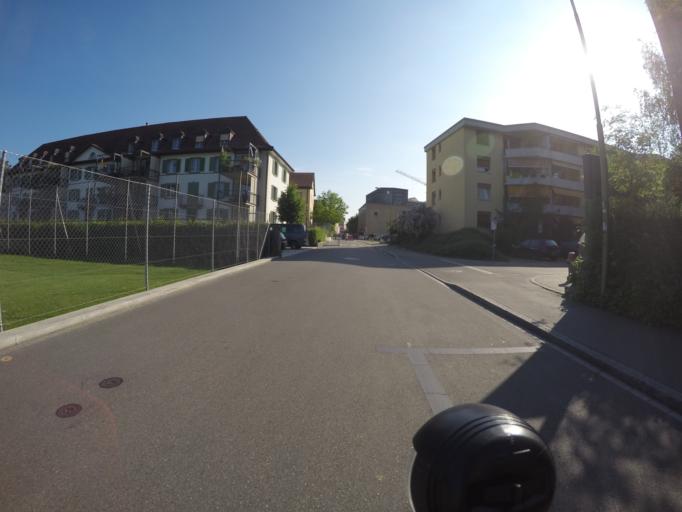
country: CH
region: Zurich
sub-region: Bezirk Winterthur
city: Stadt Winterthur (Kreis 1) / Toessfeld
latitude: 47.4925
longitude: 8.7149
